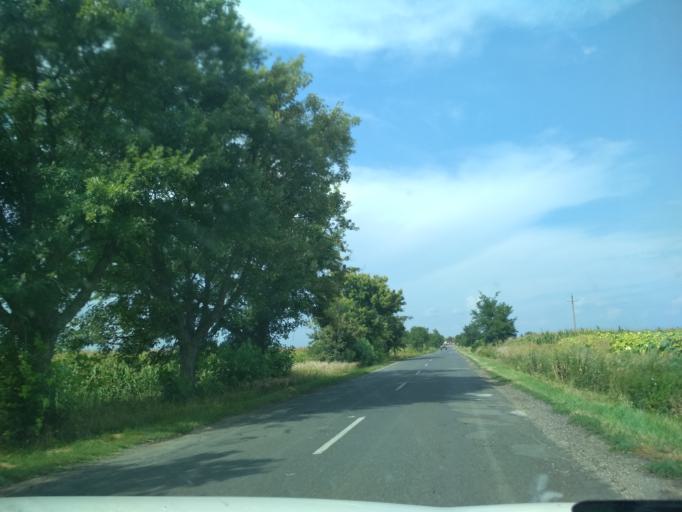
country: HU
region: Jasz-Nagykun-Szolnok
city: Tiszaszolos
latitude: 47.5431
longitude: 20.7194
